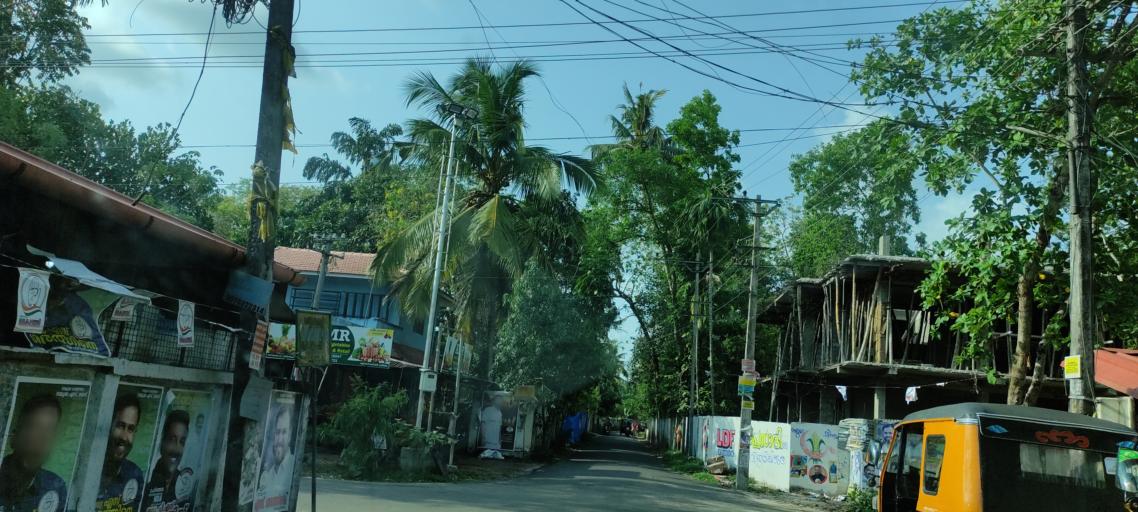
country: IN
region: Kerala
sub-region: Alappuzha
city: Vayalar
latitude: 9.6875
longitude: 76.3250
